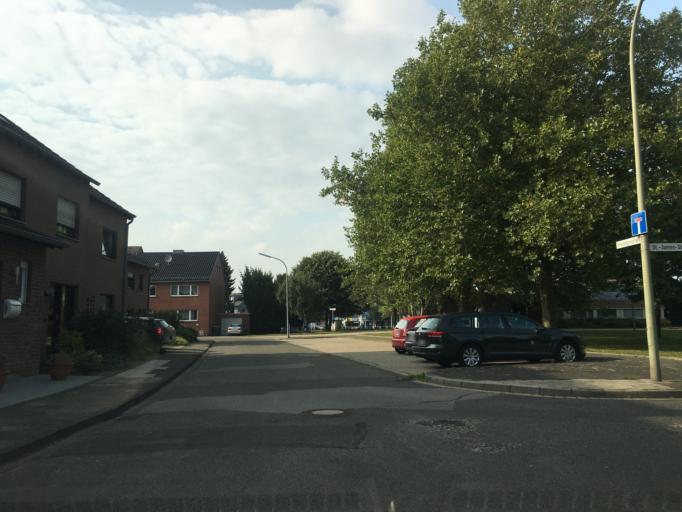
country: DE
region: North Rhine-Westphalia
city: Huckelhoven
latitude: 51.0950
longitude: 6.2167
